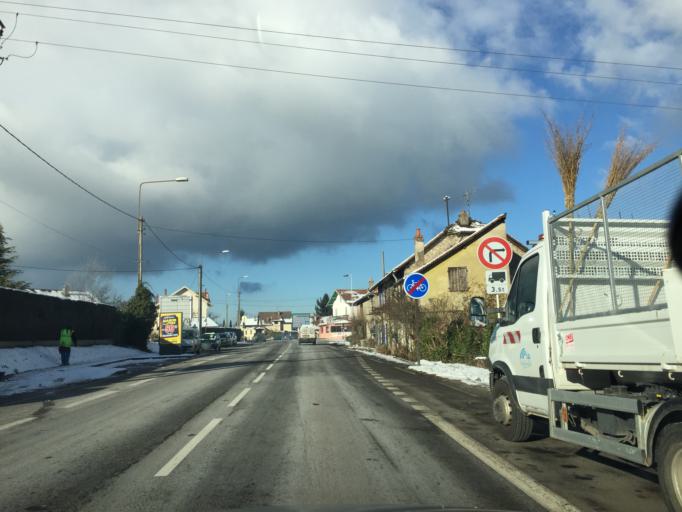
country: FR
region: Rhone-Alpes
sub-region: Departement de la Haute-Savoie
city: Thonon-les-Bains
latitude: 46.3688
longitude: 6.5012
